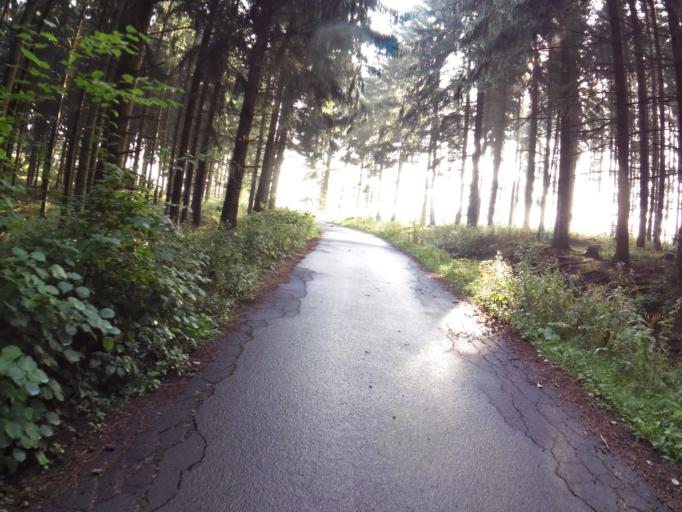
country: DE
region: North Rhine-Westphalia
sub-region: Regierungsbezirk Koln
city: Nettersheim
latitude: 50.4771
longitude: 6.5998
